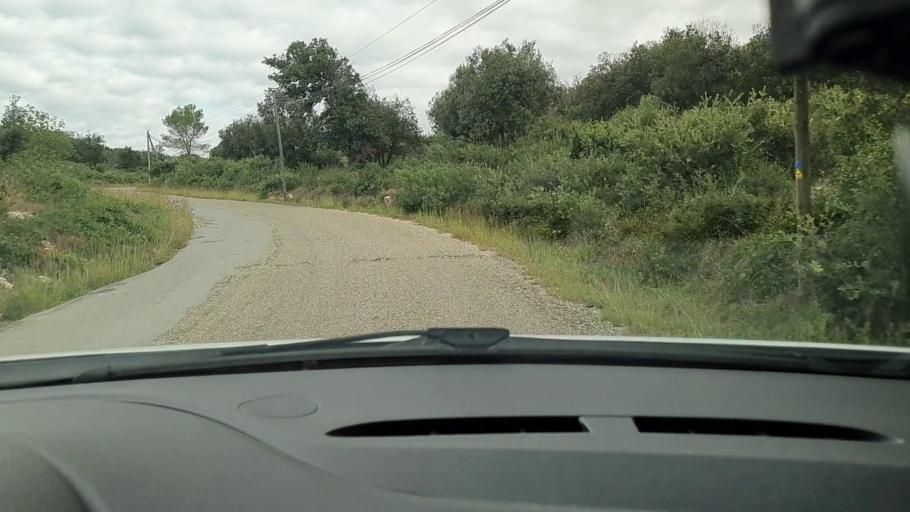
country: FR
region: Languedoc-Roussillon
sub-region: Departement du Gard
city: Montaren-et-Saint-Mediers
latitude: 44.0636
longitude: 4.3145
